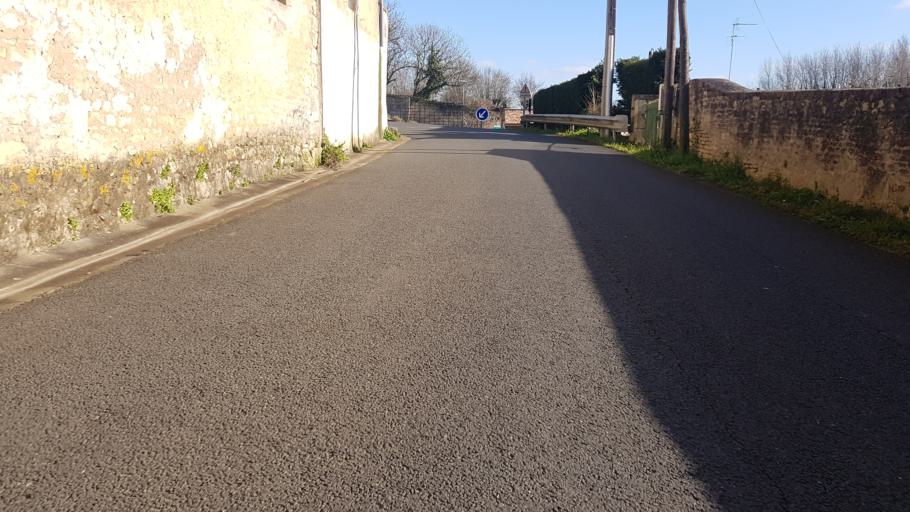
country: FR
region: Poitou-Charentes
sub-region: Departement de la Vienne
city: Chasseneuil-du-Poitou
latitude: 46.6403
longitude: 0.3513
